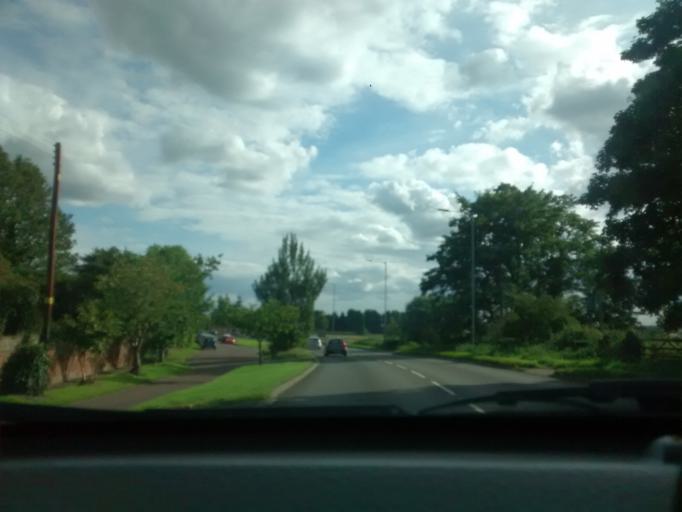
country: GB
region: England
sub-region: Norfolk
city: King's Lynn
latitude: 52.6938
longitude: 0.4196
